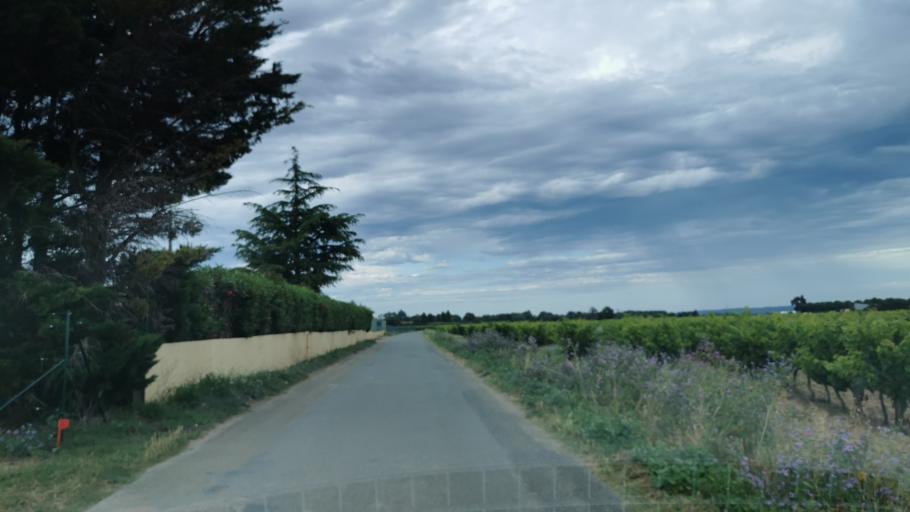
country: FR
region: Languedoc-Roussillon
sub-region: Departement de l'Aude
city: Moussan
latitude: 43.2453
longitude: 2.9746
